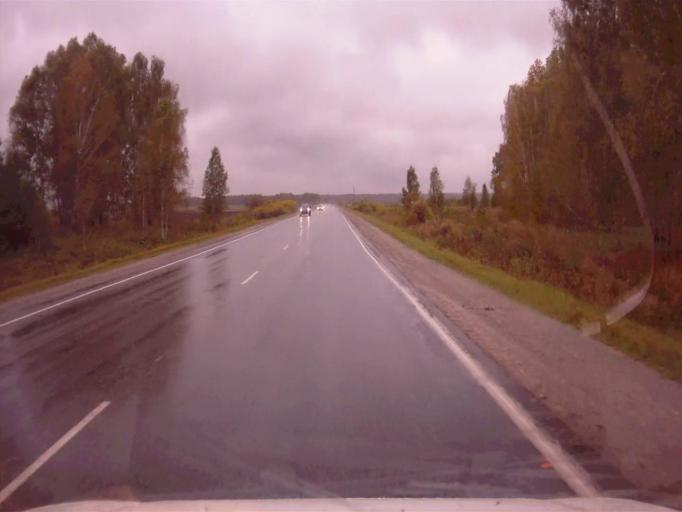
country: RU
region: Chelyabinsk
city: Argayash
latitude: 55.4790
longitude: 60.8193
